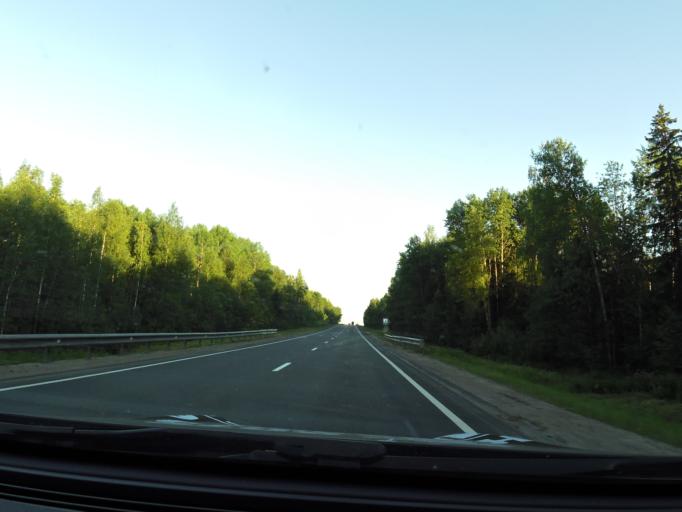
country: RU
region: Vologda
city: Gryazovets
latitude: 58.6669
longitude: 40.3126
